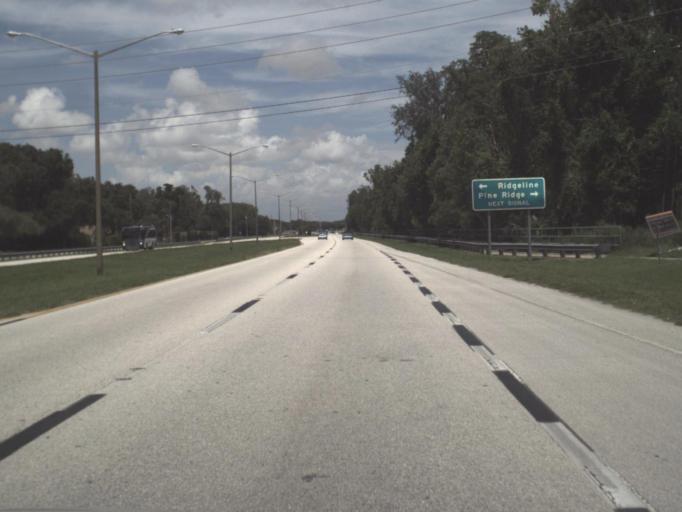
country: US
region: Florida
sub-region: Pinellas County
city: East Lake
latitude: 28.1190
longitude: -82.6951
